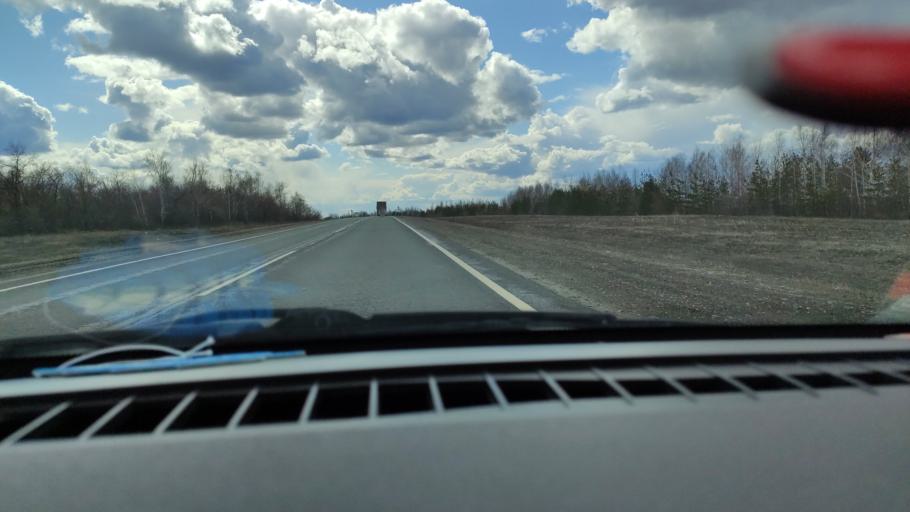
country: RU
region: Samara
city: Syzran'
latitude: 52.8635
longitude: 48.2682
